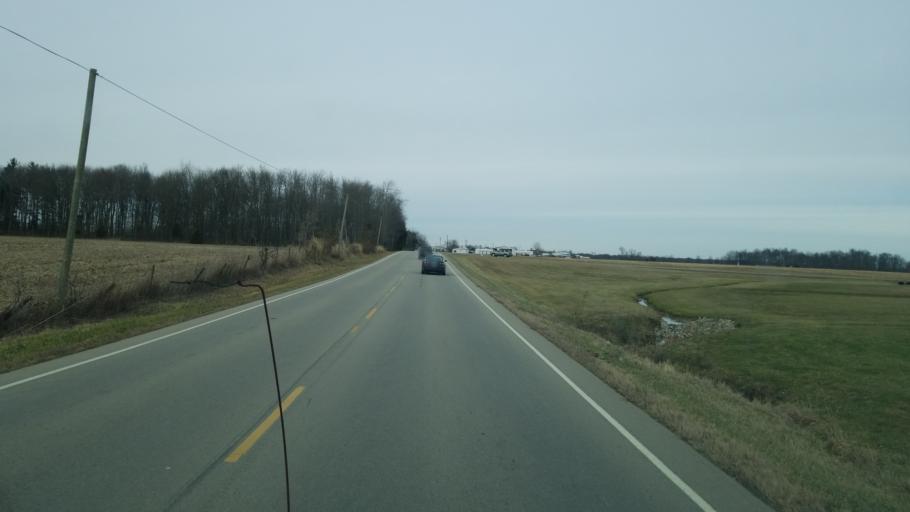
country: US
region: Ohio
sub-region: Adams County
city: Winchester
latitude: 39.0570
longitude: -83.7036
